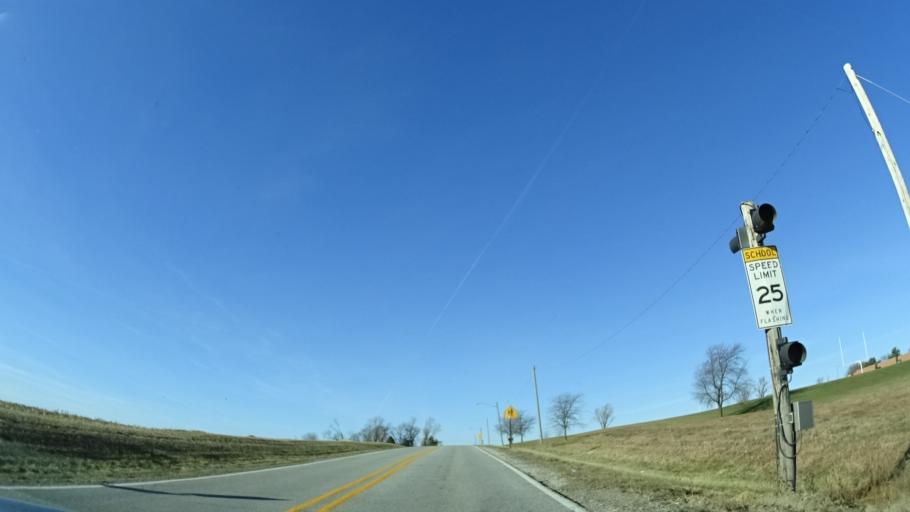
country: US
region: Nebraska
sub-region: Sarpy County
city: Springfield
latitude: 41.0890
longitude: -96.0769
